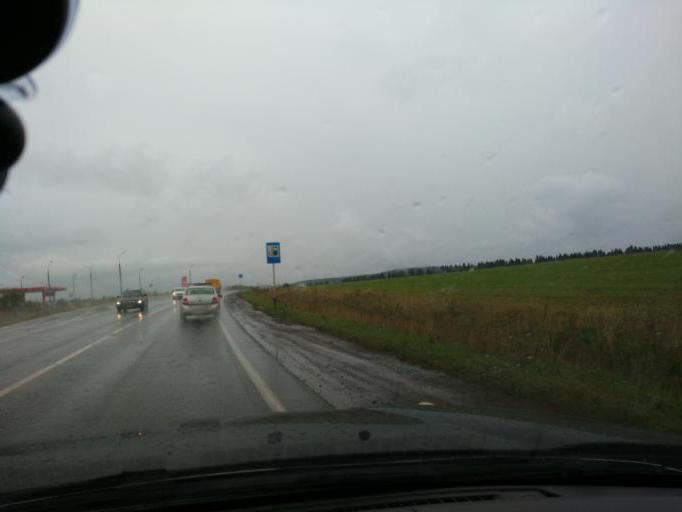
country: RU
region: Perm
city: Yugo-Kamskiy
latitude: 57.6922
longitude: 55.5845
